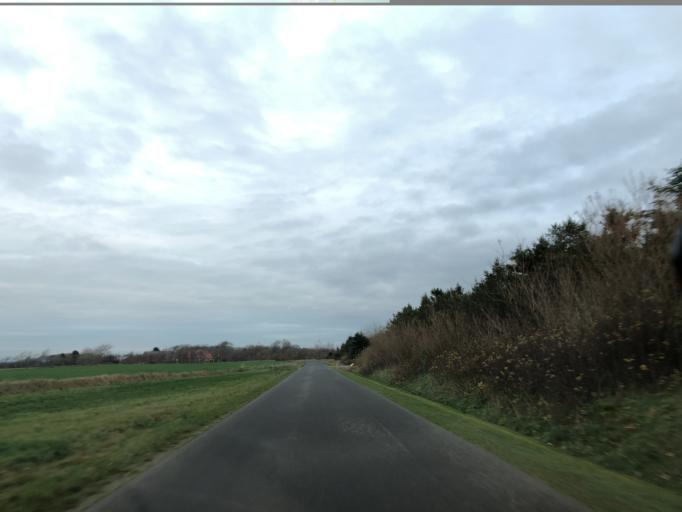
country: DK
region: Central Jutland
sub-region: Holstebro Kommune
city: Ulfborg
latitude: 56.2729
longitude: 8.2638
